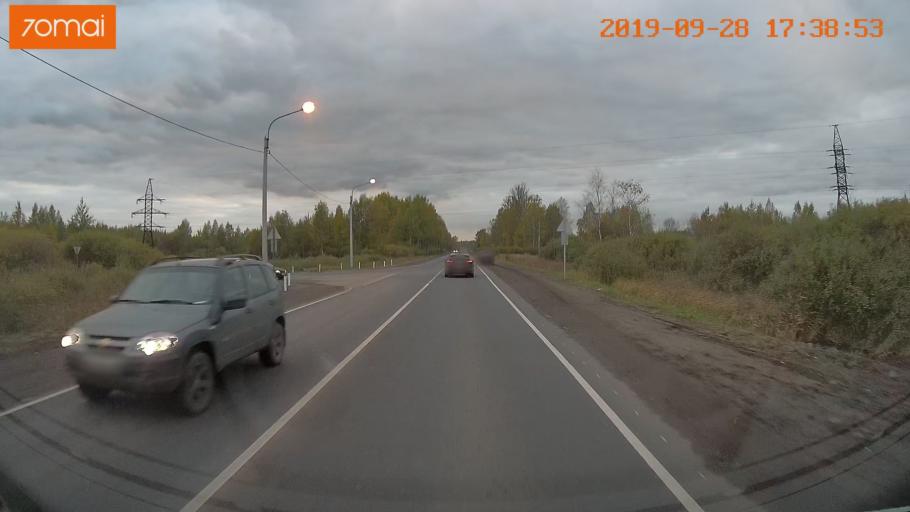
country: RU
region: Jaroslavl
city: Yaroslavl
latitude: 57.5437
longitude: 39.9334
